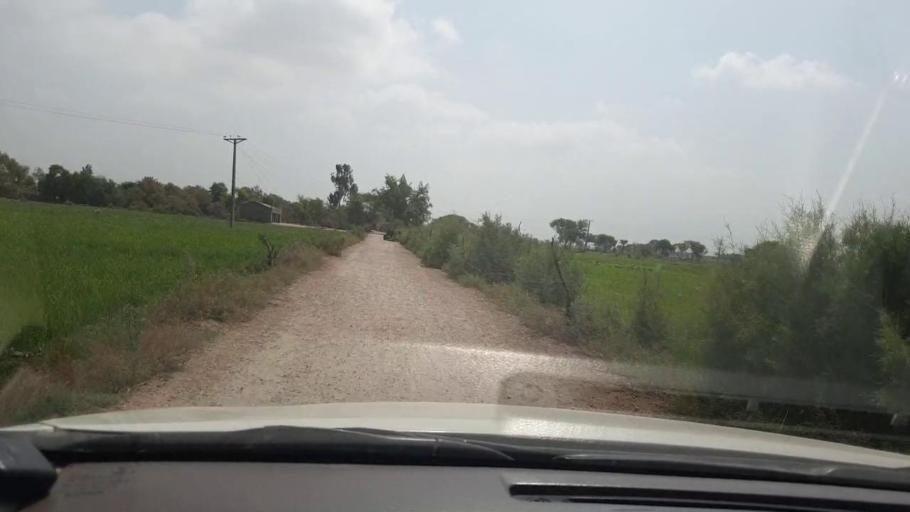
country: PK
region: Sindh
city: Garhi Yasin
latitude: 28.0183
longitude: 68.5289
